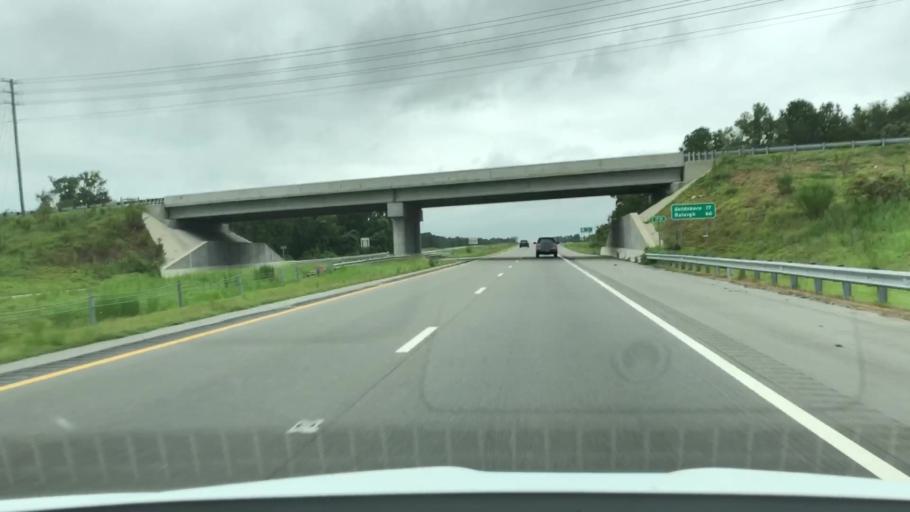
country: US
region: North Carolina
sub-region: Lenoir County
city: La Grange
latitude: 35.3109
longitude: -77.8242
